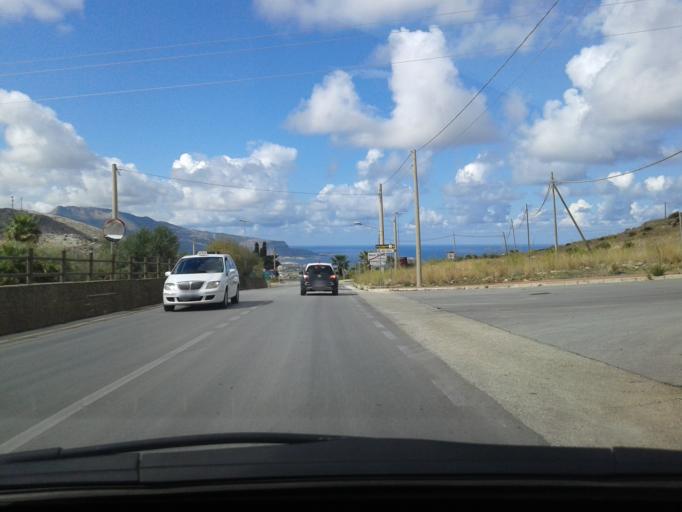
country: IT
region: Sicily
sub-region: Trapani
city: Custonaci
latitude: 38.0764
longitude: 12.6939
